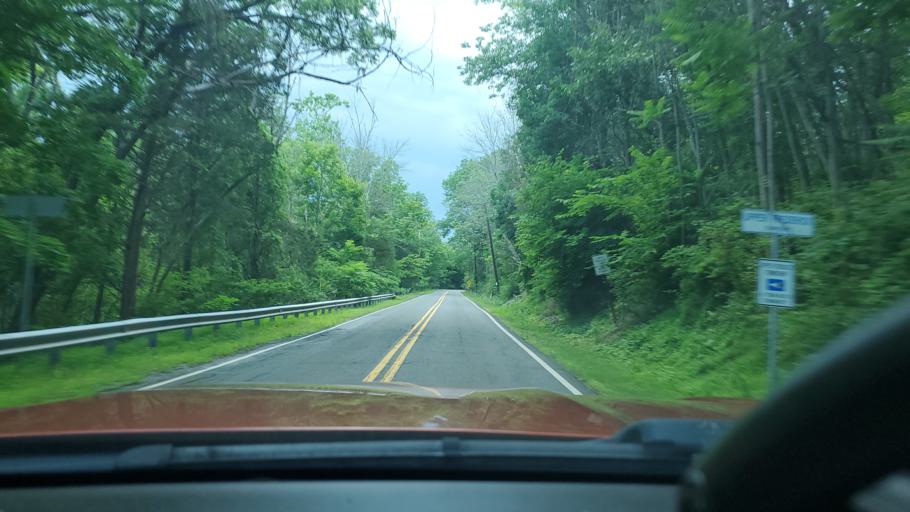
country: US
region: Pennsylvania
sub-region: Montgomery County
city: Limerick
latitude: 40.2734
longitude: -75.5183
